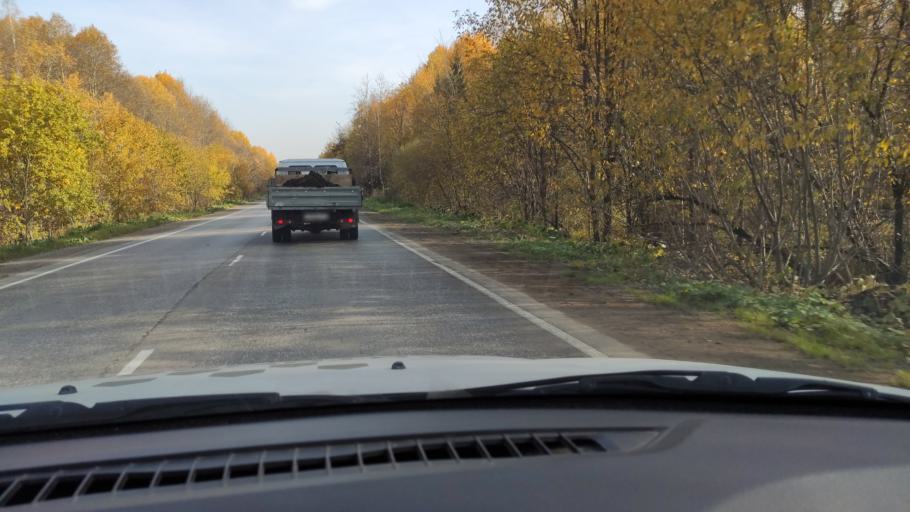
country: RU
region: Perm
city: Novyye Lyady
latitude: 58.0220
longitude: 56.6574
